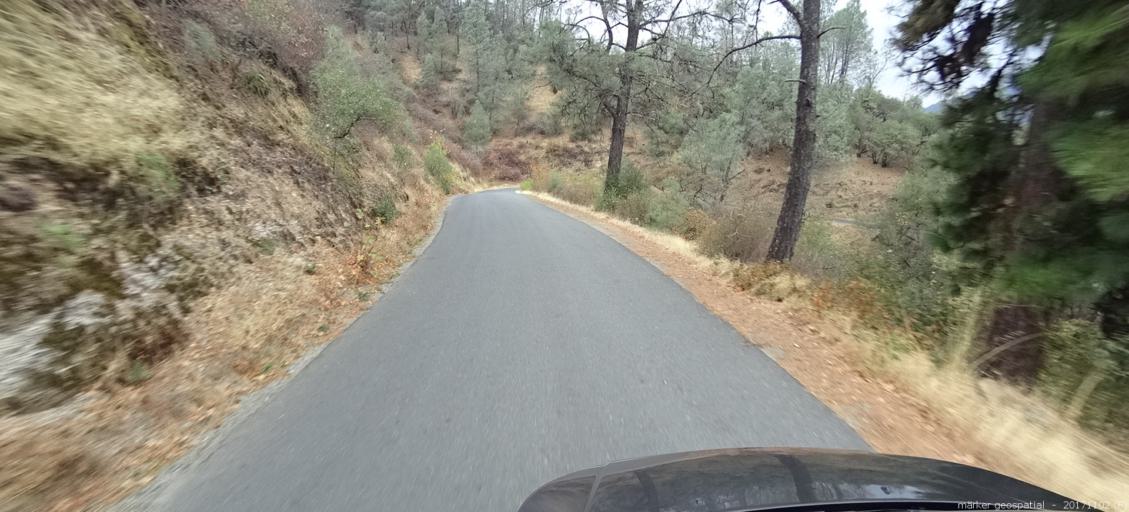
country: US
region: California
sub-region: Shasta County
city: Bella Vista
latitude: 40.7510
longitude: -122.2452
